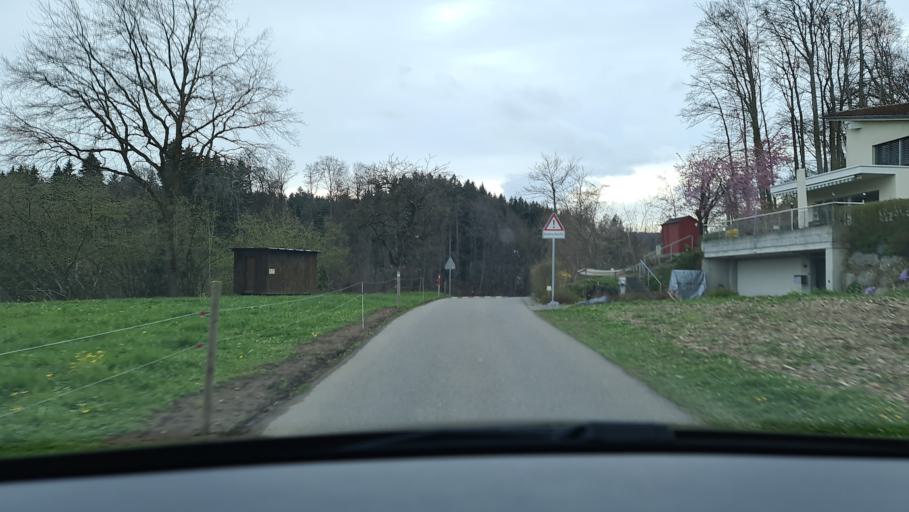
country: CH
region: Aargau
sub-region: Bezirk Muri
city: Sins
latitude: 47.1947
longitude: 8.3860
